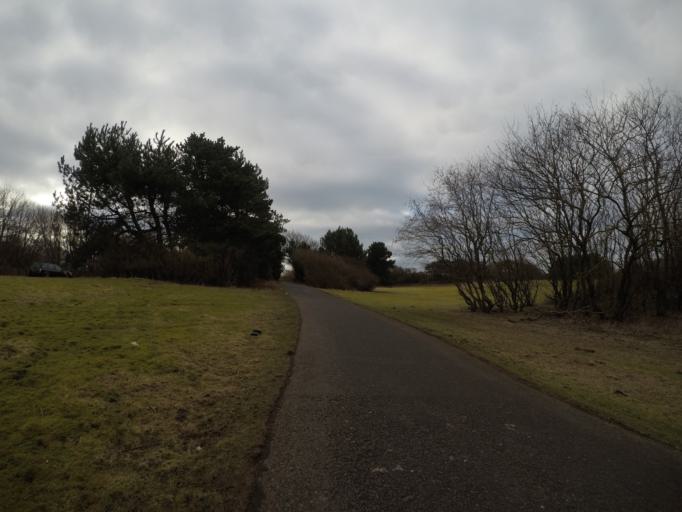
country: GB
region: Scotland
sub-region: North Ayrshire
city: Irvine
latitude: 55.6032
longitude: -4.6810
